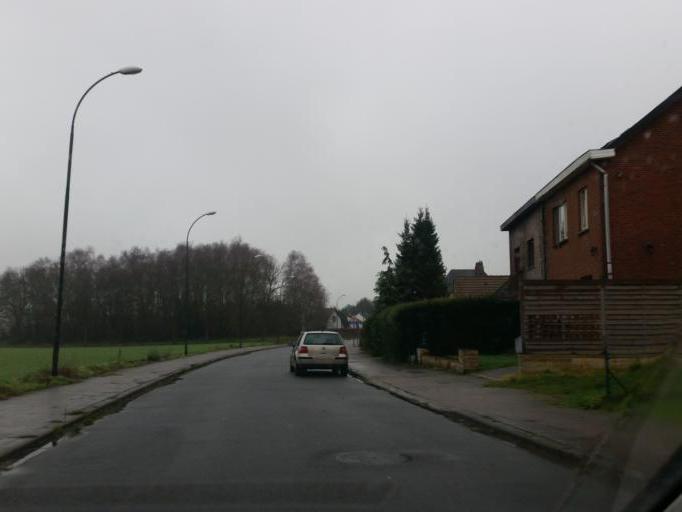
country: BE
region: Flanders
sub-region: Provincie Vlaams-Brabant
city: Zemst
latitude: 50.9514
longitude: 4.4749
